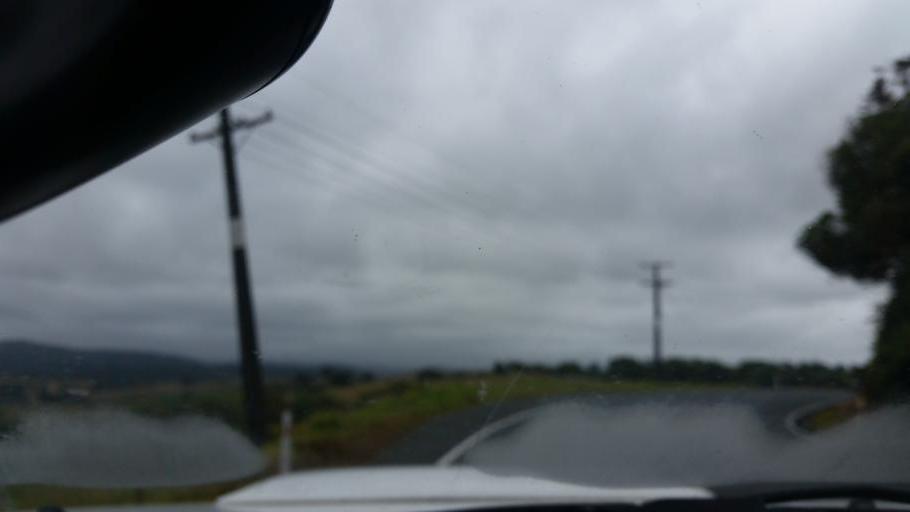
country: NZ
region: Auckland
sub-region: Auckland
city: Wellsford
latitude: -36.1519
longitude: 174.4726
